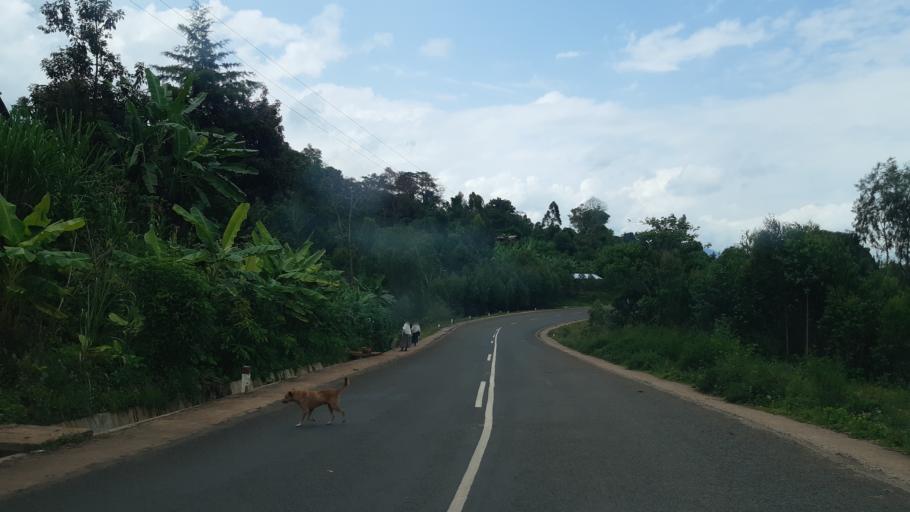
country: ET
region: Southern Nations, Nationalities, and People's Region
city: Bonga
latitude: 7.2446
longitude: 36.2572
